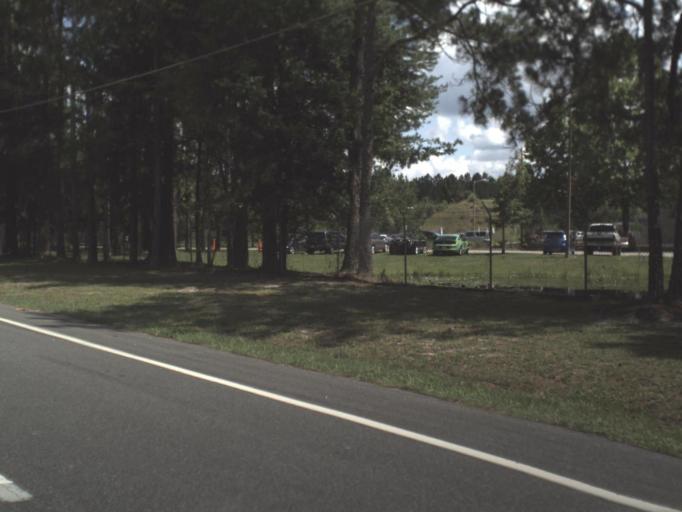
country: US
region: Florida
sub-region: Alachua County
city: Gainesville
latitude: 29.6772
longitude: -82.2742
